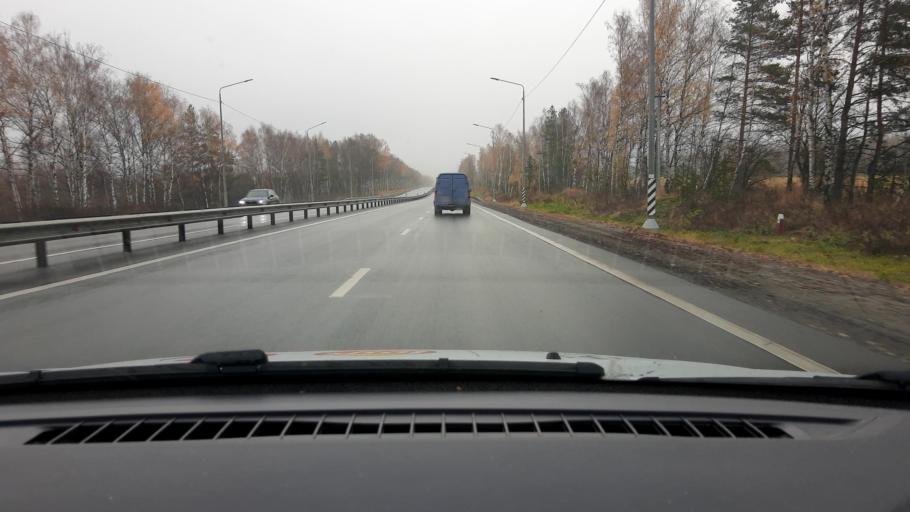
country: RU
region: Nizjnij Novgorod
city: Burevestnik
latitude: 56.0616
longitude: 43.9431
